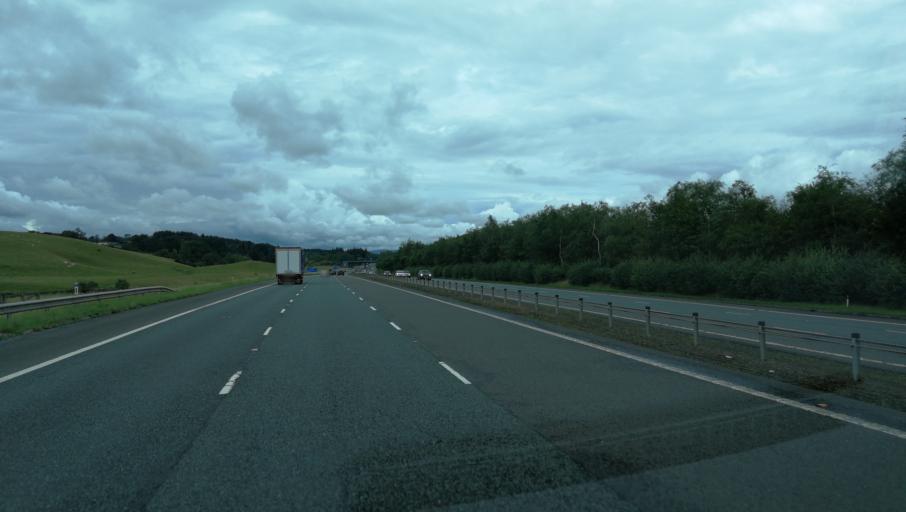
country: GB
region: Scotland
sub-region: Dumfries and Galloway
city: Lochmaben
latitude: 55.2015
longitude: -3.4116
